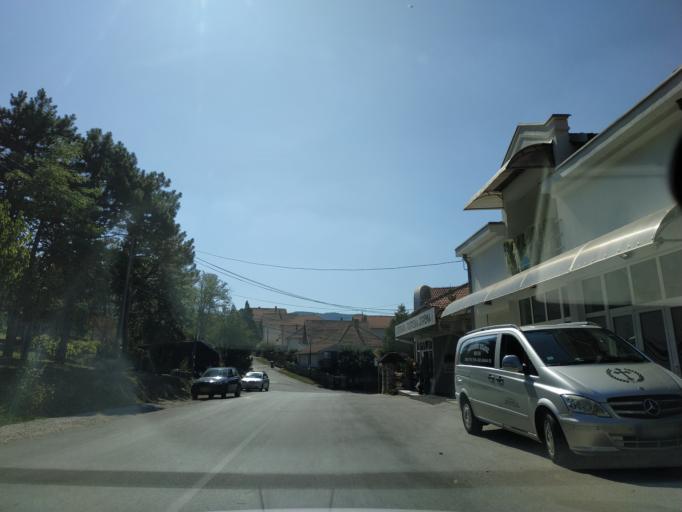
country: RS
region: Central Serbia
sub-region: Sumadijski Okrug
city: Arangelovac
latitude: 44.2991
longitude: 20.5777
